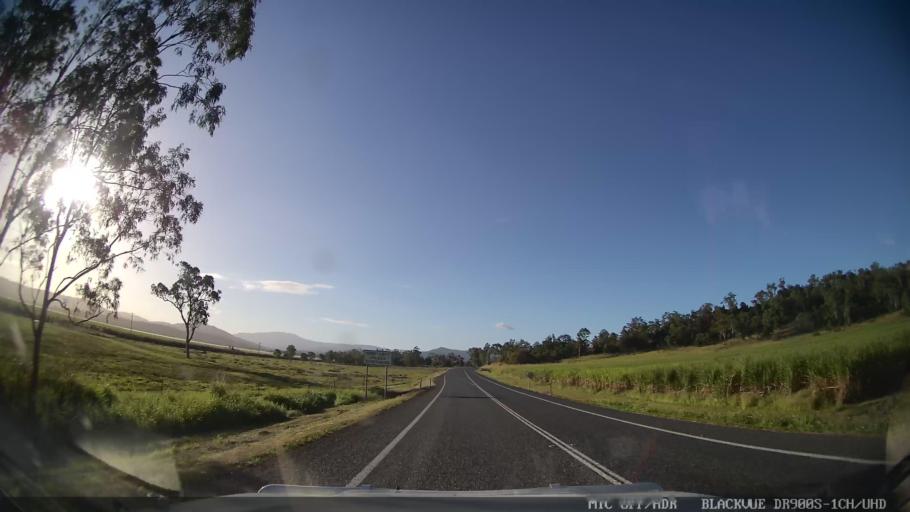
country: AU
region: Queensland
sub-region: Whitsunday
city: Proserpine
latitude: -20.3668
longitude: 148.6224
